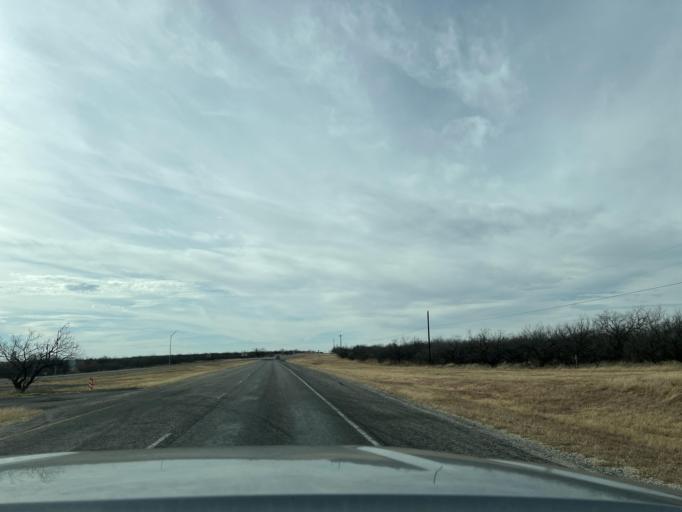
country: US
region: Texas
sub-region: Shackelford County
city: Albany
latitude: 32.7076
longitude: -99.4257
